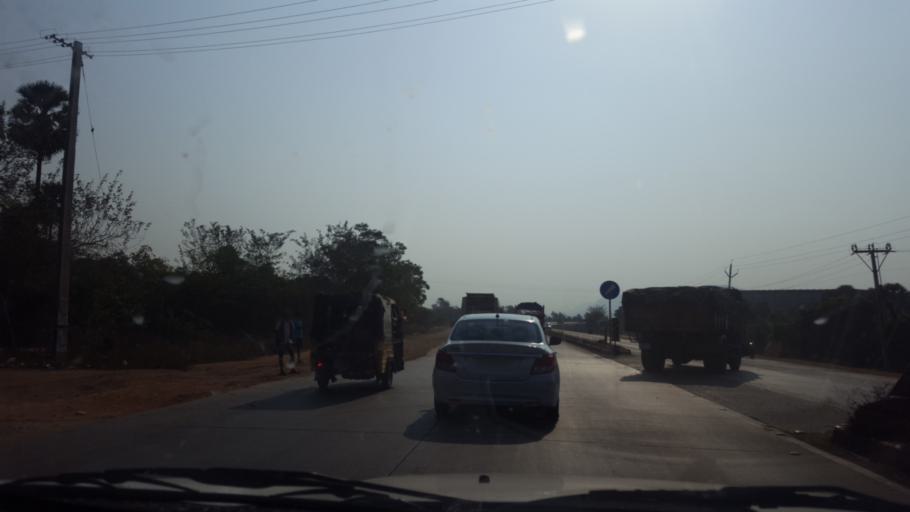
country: IN
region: Andhra Pradesh
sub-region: Vishakhapatnam
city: Anakapalle
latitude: 17.6532
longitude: 82.9262
